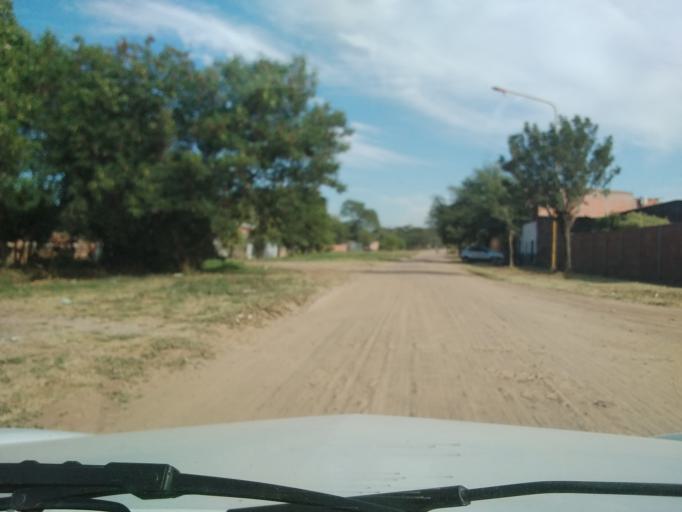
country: AR
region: Corrientes
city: Corrientes
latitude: -27.5055
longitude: -58.8056
